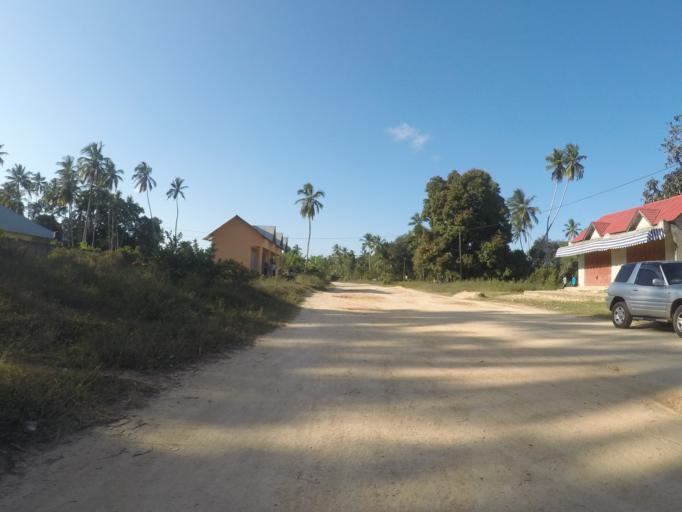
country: TZ
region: Zanzibar Central/South
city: Koani
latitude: -6.1554
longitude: 39.2873
